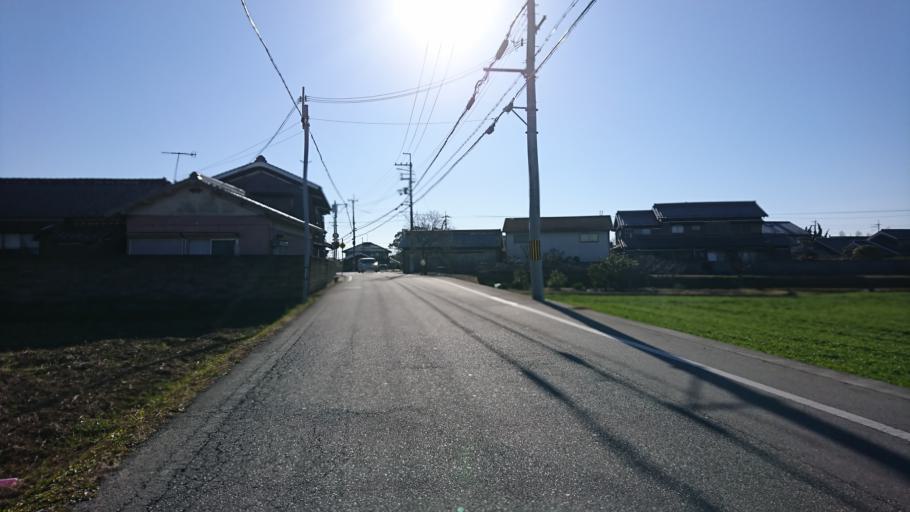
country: JP
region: Hyogo
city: Miki
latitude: 34.7439
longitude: 134.9396
